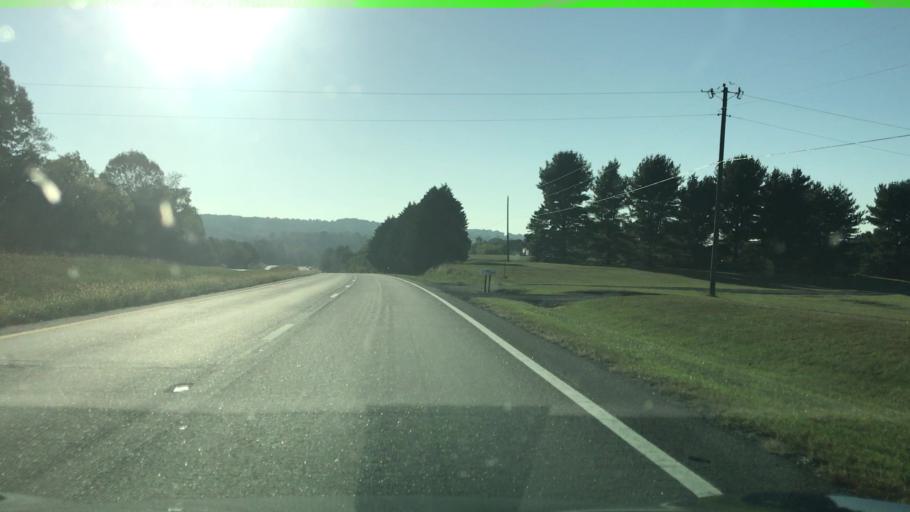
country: US
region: Virginia
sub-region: City of Bedford
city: Bedford
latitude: 37.3129
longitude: -79.4048
